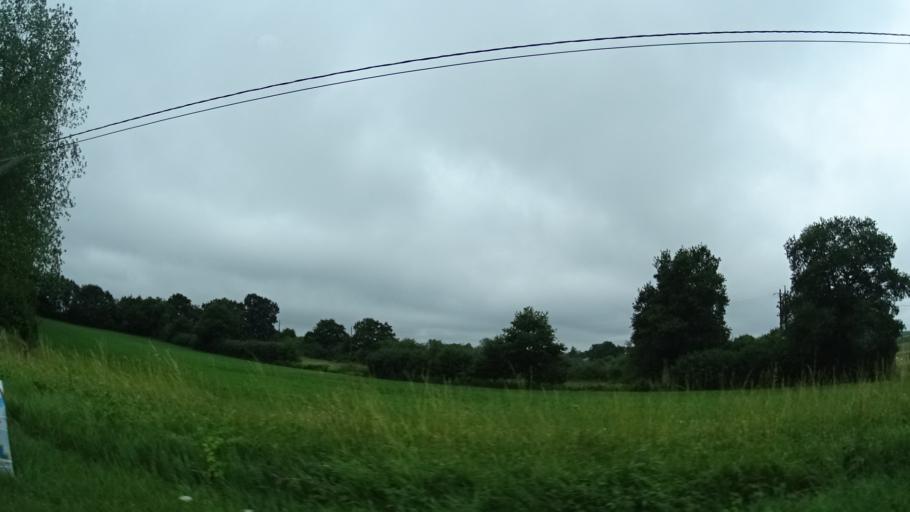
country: BE
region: Wallonia
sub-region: Province du Luxembourg
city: Habay-la-Vieille
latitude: 49.7143
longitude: 5.6892
